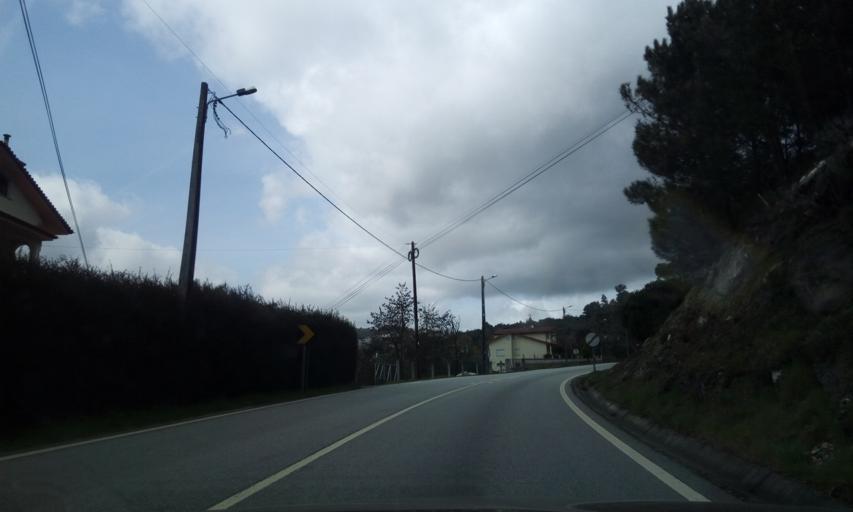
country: PT
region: Viseu
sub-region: Mangualde
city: Mangualde
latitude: 40.6323
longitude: -7.7421
